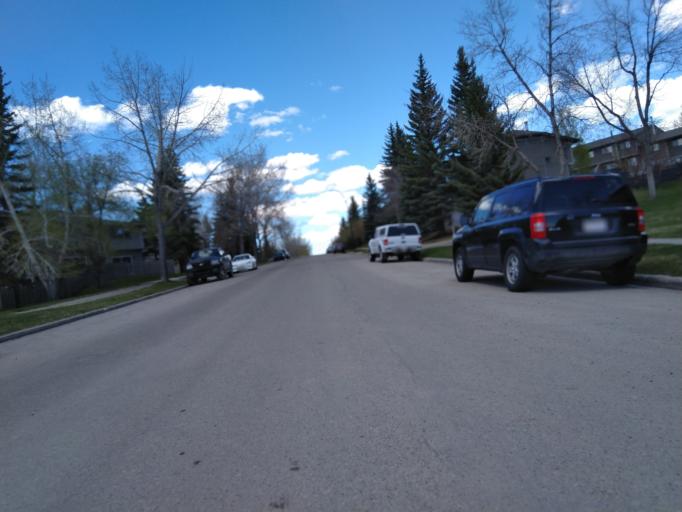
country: CA
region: Alberta
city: Calgary
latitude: 51.0104
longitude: -114.1597
